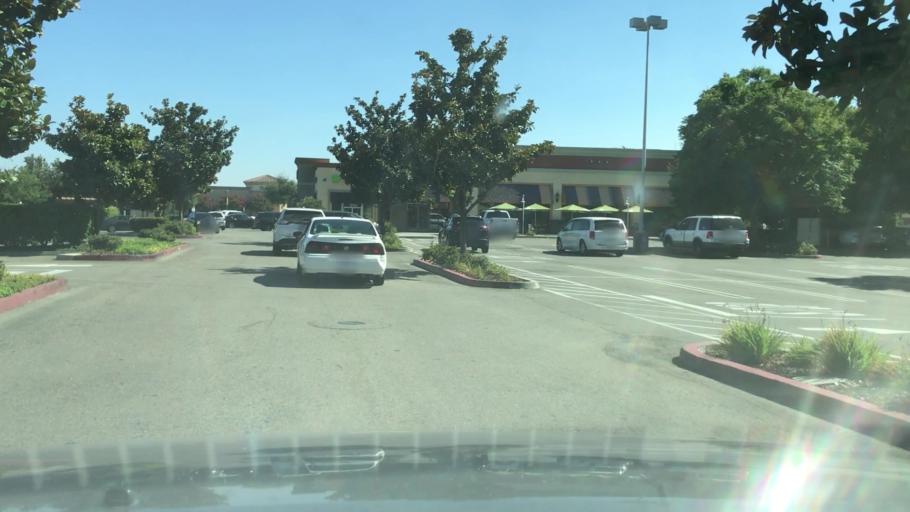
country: US
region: California
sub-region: San Joaquin County
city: Lincoln Village
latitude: 38.0550
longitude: -121.3750
